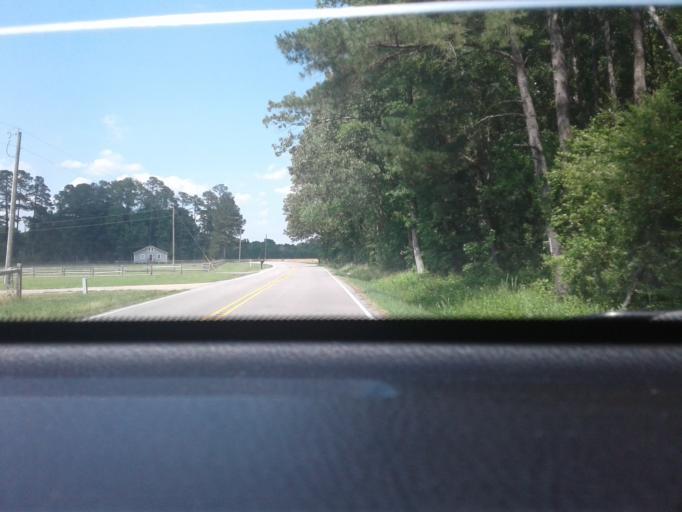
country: US
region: North Carolina
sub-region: Harnett County
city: Erwin
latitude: 35.2271
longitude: -78.6823
